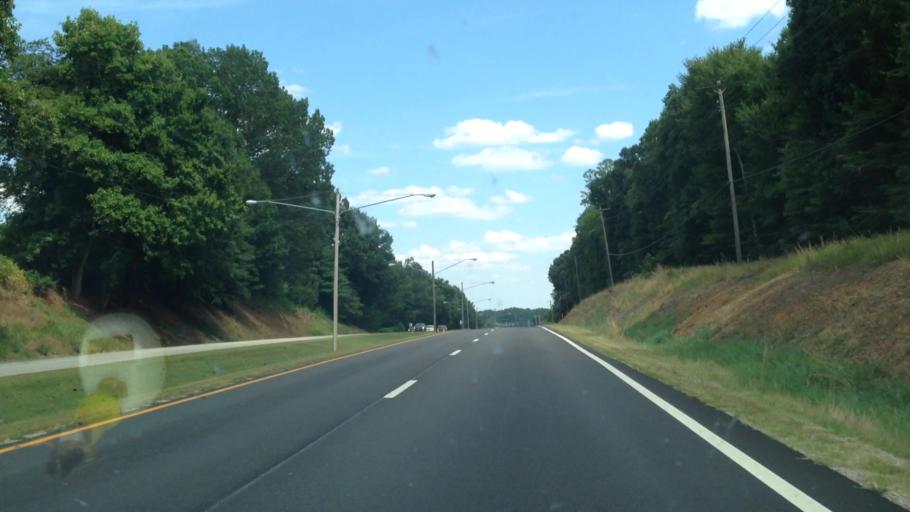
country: US
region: Virginia
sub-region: City of Danville
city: Danville
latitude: 36.5956
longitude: -79.4708
